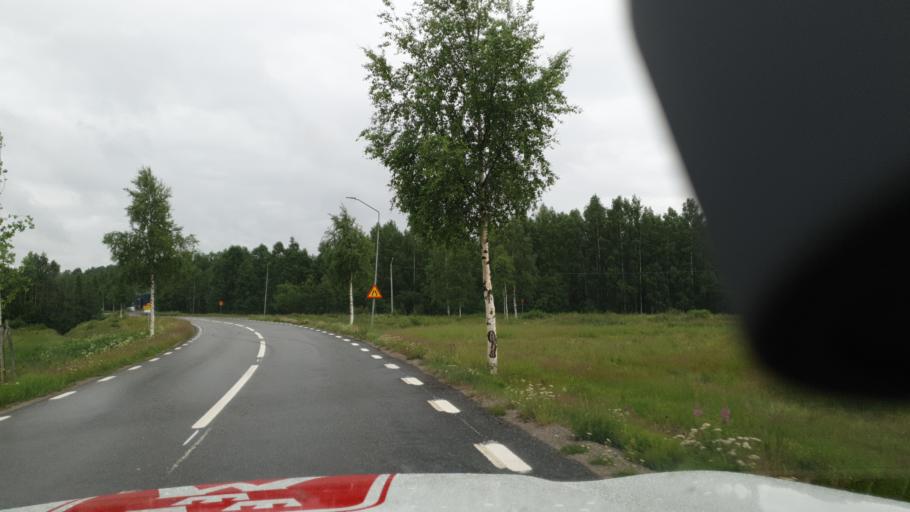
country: SE
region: Vaesterbotten
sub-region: Vannas Kommun
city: Vannasby
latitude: 63.8514
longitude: 19.9098
